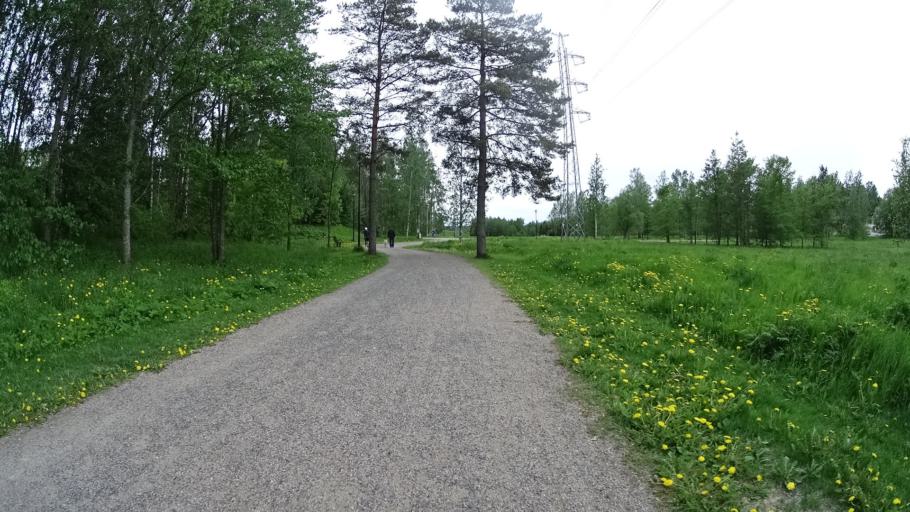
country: FI
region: Uusimaa
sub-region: Helsinki
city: Vantaa
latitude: 60.2838
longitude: 25.0583
